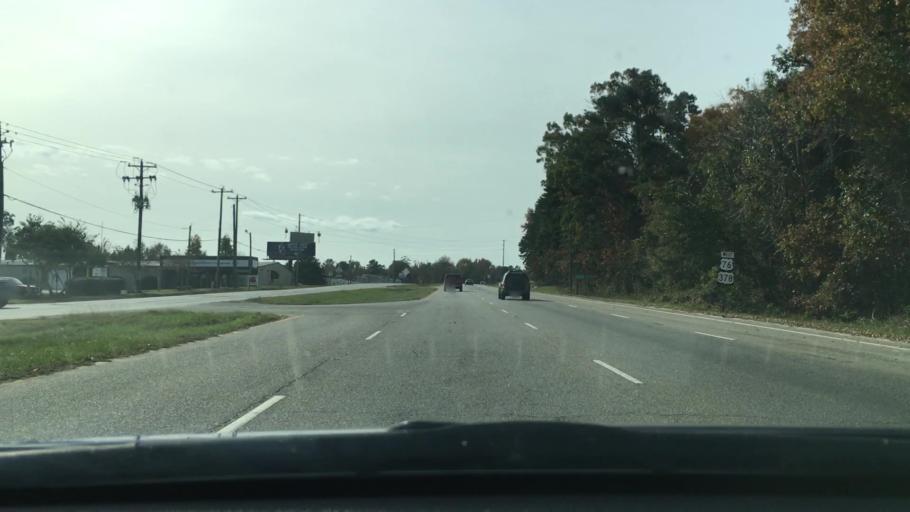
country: US
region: South Carolina
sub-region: Sumter County
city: Oakland
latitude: 33.9509
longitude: -80.4987
